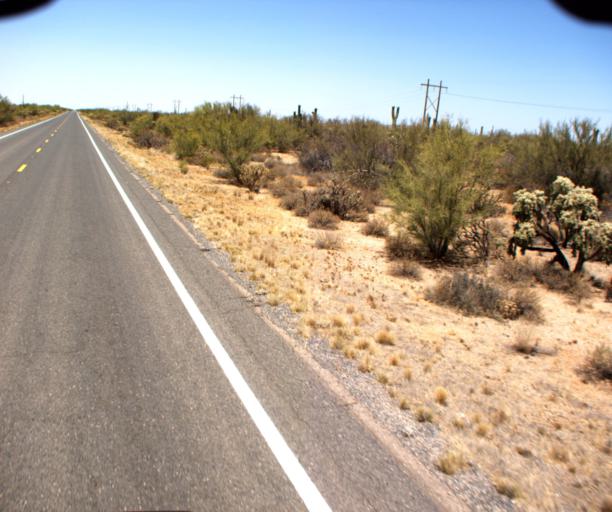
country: US
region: Arizona
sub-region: Pinal County
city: Florence
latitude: 32.8157
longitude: -111.1974
